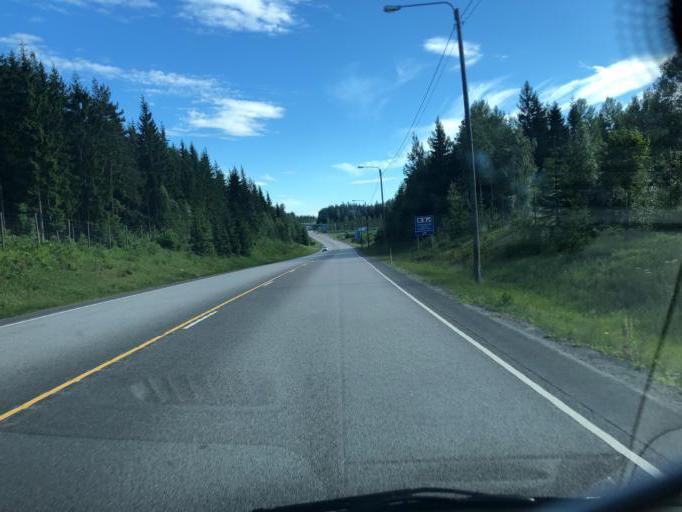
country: FI
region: Uusimaa
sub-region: Loviisa
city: Perna
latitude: 60.5041
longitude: 25.9649
